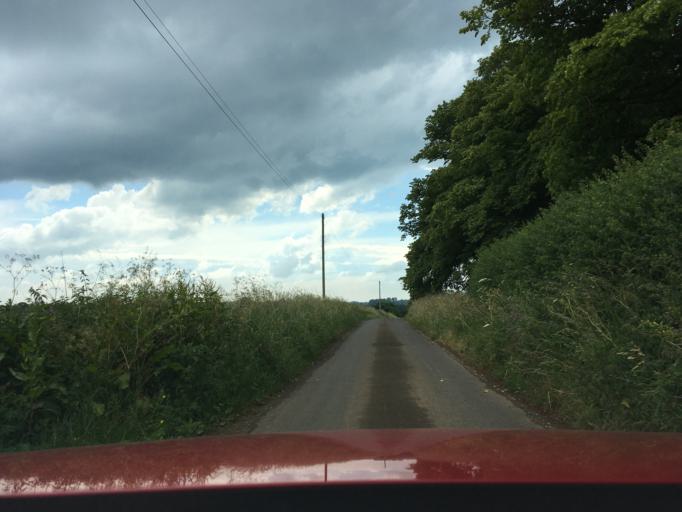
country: GB
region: England
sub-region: Gloucestershire
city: Shurdington
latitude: 51.7972
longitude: -2.0706
